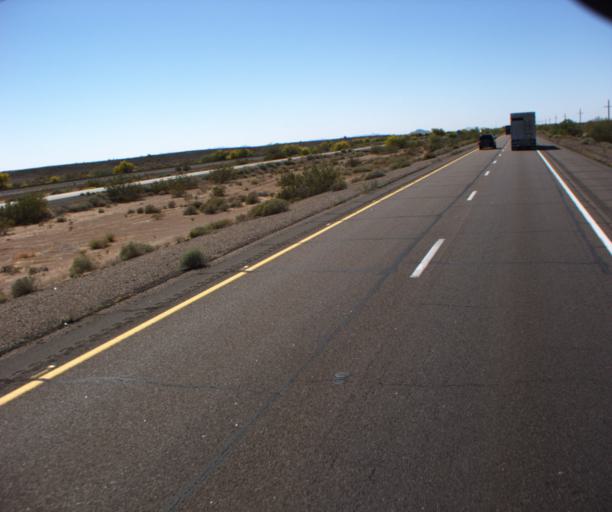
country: US
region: Arizona
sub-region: Maricopa County
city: Gila Bend
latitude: 32.8422
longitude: -113.3076
